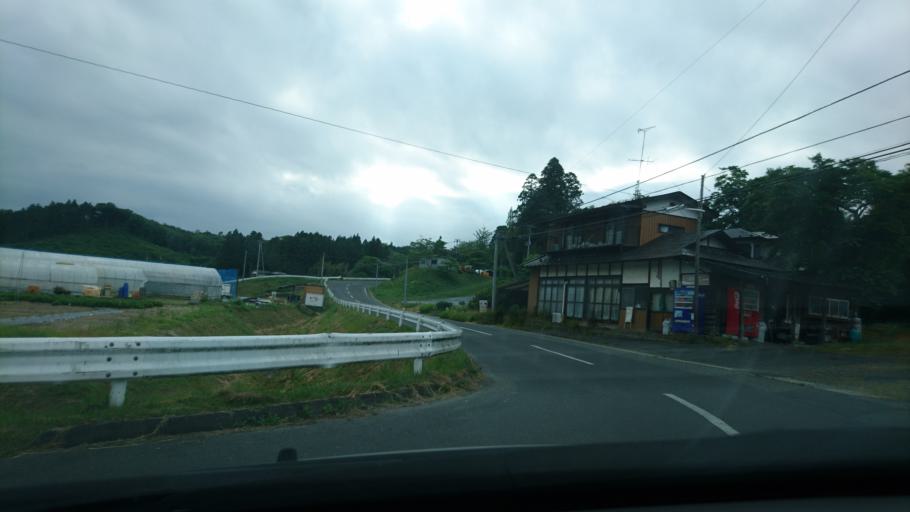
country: JP
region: Iwate
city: Ichinoseki
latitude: 38.8997
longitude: 141.1574
